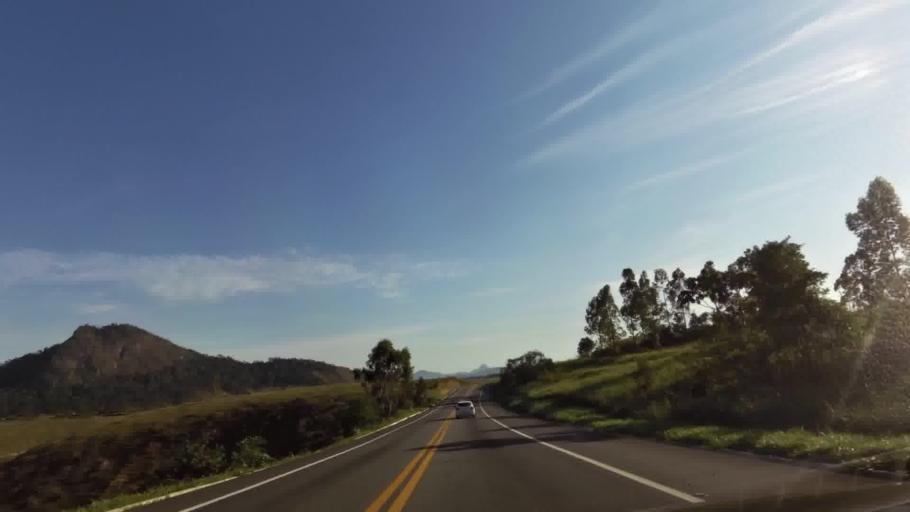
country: BR
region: Espirito Santo
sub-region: Viana
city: Viana
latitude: -20.4914
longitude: -40.4771
